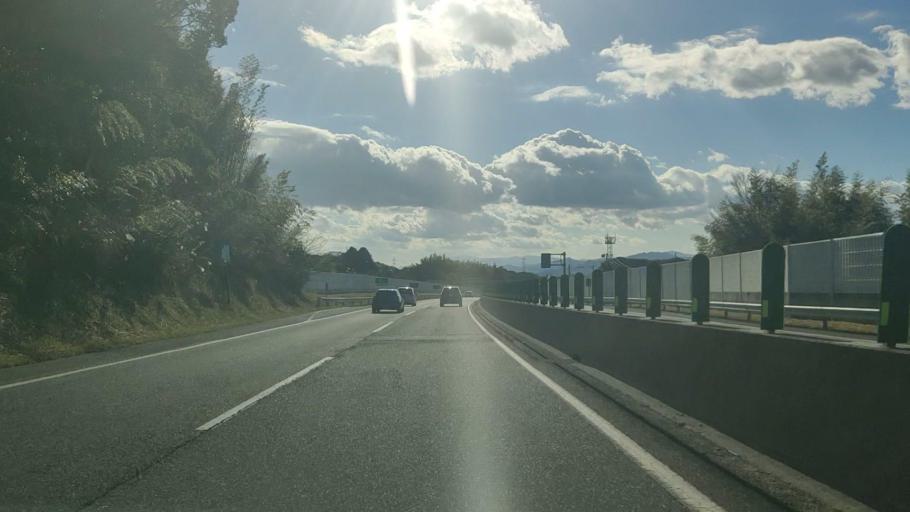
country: JP
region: Fukuoka
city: Nakama
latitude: 33.8267
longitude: 130.7641
